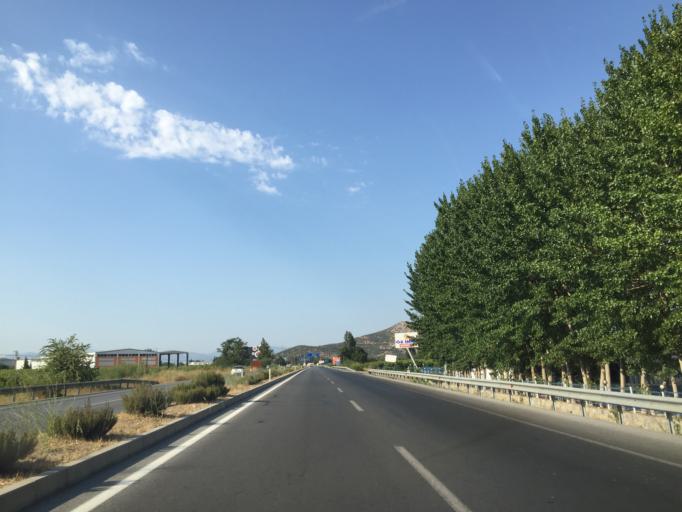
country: TR
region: Izmir
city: Belevi
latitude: 38.0155
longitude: 27.4375
